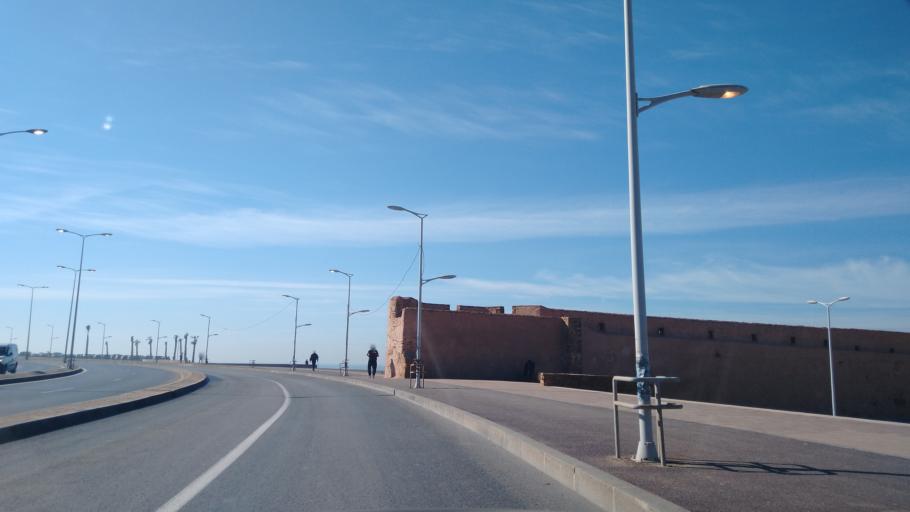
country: MA
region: Rabat-Sale-Zemmour-Zaer
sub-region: Rabat
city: Rabat
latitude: 34.0309
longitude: -6.8439
